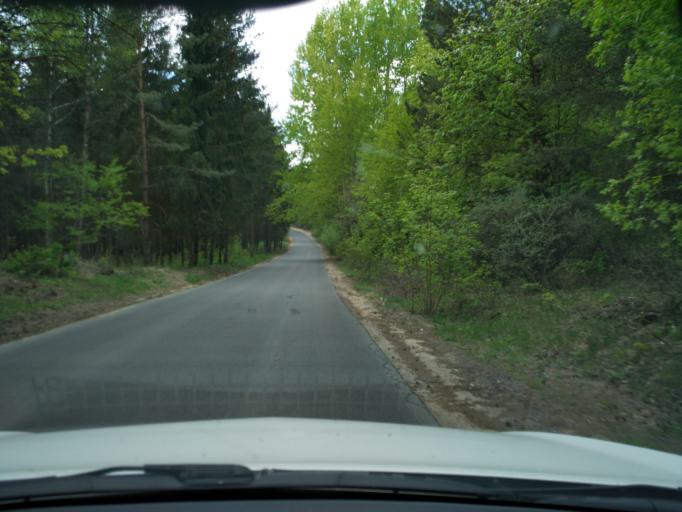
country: LT
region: Vilnius County
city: Rasos
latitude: 54.6940
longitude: 25.3381
